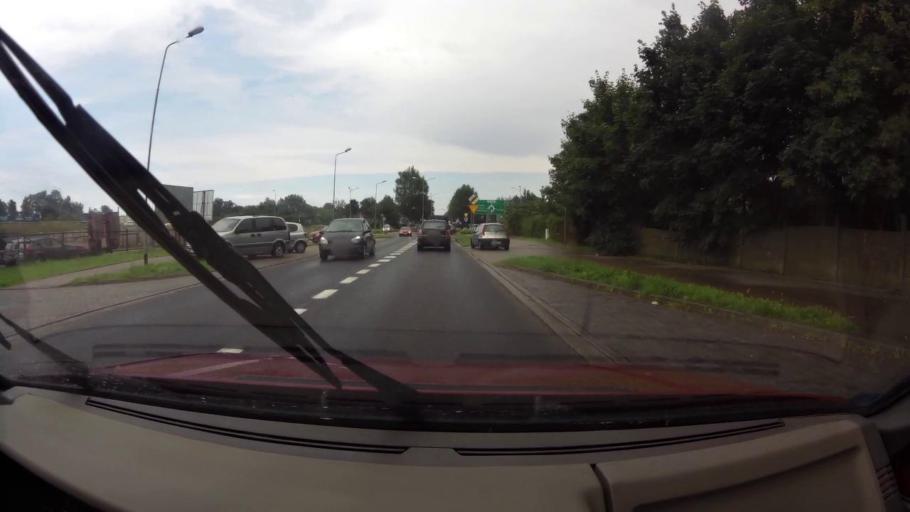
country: PL
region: West Pomeranian Voivodeship
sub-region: Koszalin
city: Koszalin
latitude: 54.1794
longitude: 16.1691
